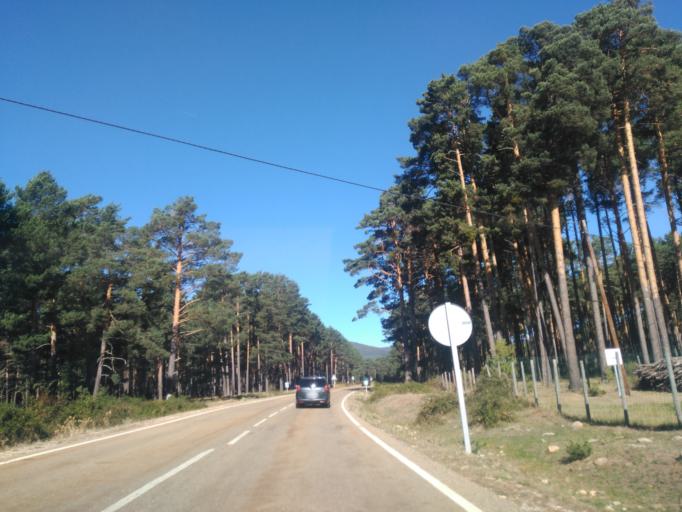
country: ES
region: Castille and Leon
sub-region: Provincia de Soria
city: Vinuesa
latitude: 41.9678
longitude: -2.7829
